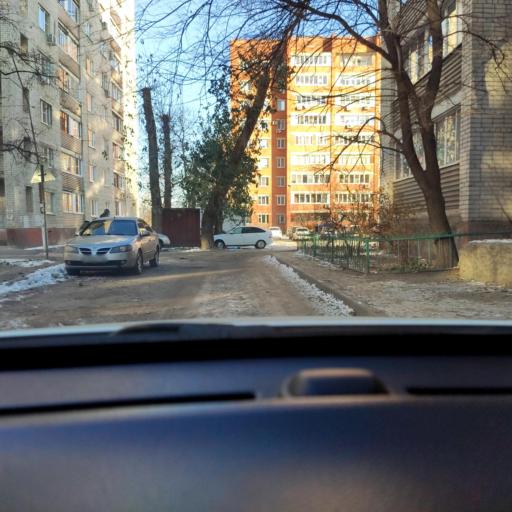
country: RU
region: Voronezj
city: Voronezh
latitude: 51.6421
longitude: 39.2750
